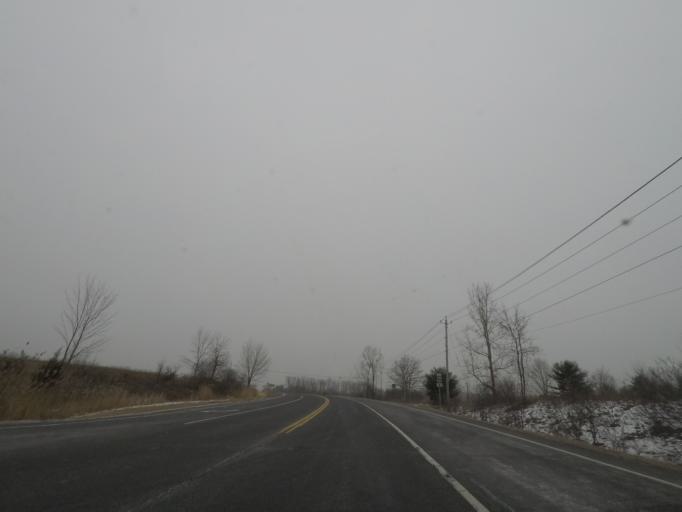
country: US
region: New York
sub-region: Albany County
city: Delmar
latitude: 42.5626
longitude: -73.8243
